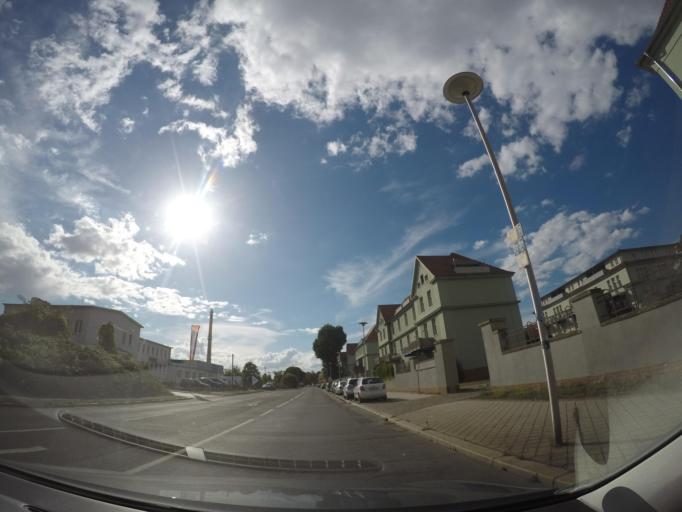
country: DE
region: Saxony-Anhalt
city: Diesdorf
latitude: 52.1225
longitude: 11.5954
